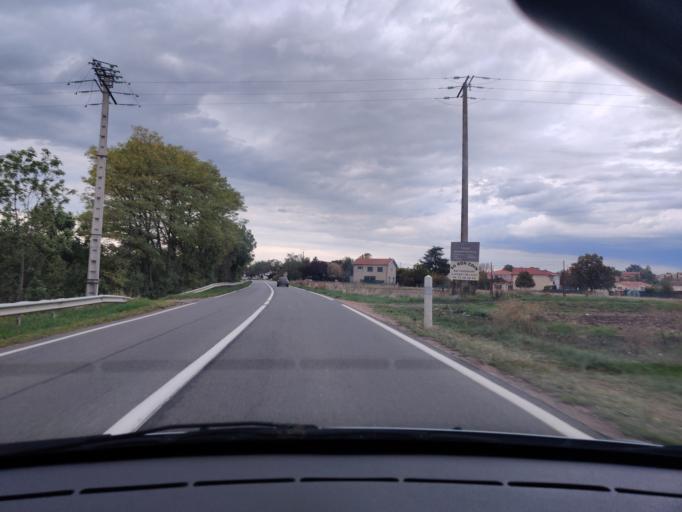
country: FR
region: Auvergne
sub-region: Departement du Puy-de-Dome
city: Saint-Bonnet-pres-Riom
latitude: 45.9231
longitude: 3.1206
